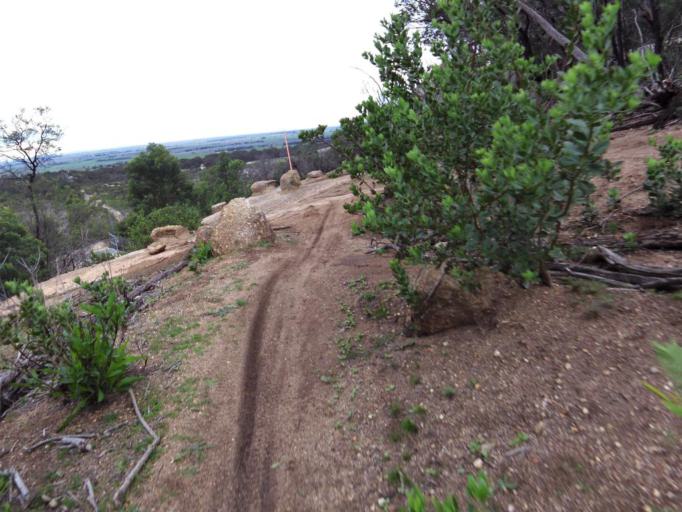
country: AU
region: Victoria
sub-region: Wyndham
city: Little River
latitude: -37.9308
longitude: 144.4379
